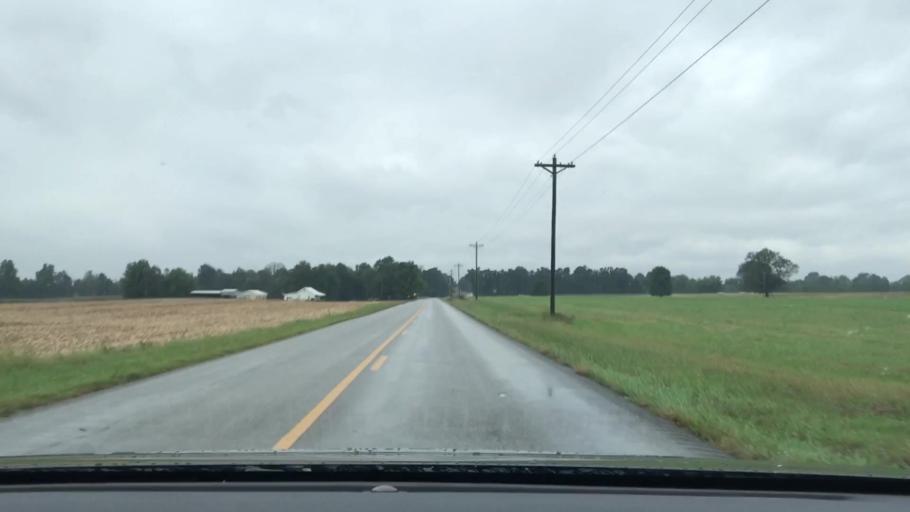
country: US
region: Kentucky
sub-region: McLean County
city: Calhoun
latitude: 37.4035
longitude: -87.2652
